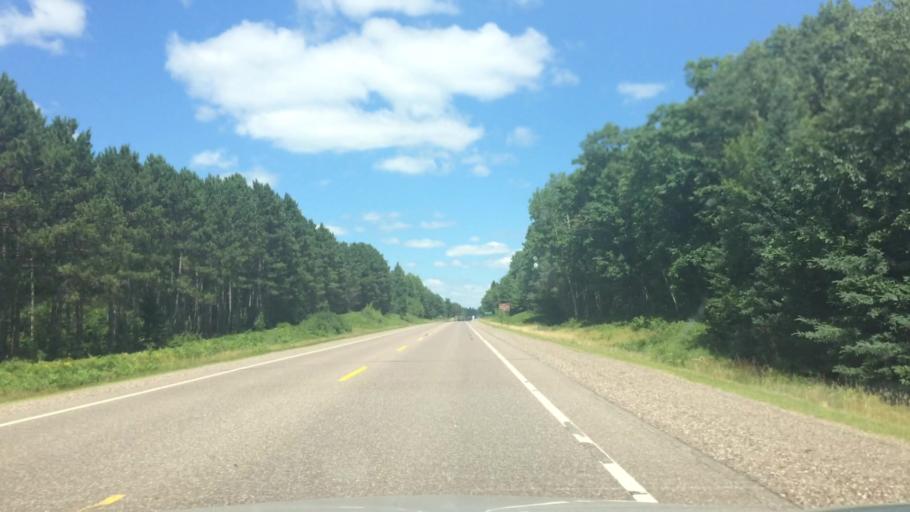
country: US
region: Wisconsin
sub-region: Vilas County
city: Lac du Flambeau
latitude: 45.9667
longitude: -89.6999
